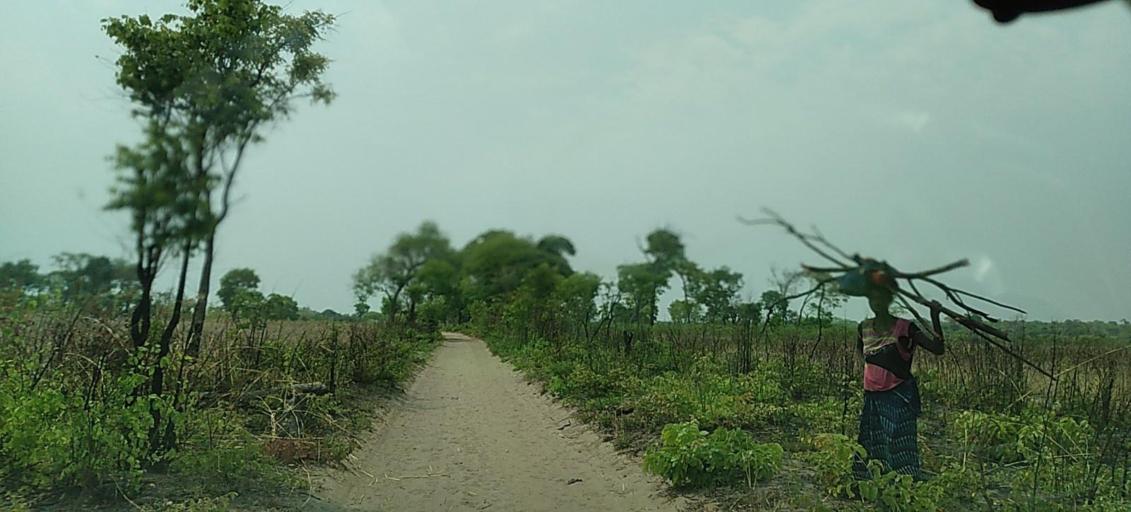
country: ZM
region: North-Western
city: Kabompo
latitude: -13.4714
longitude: 24.4473
